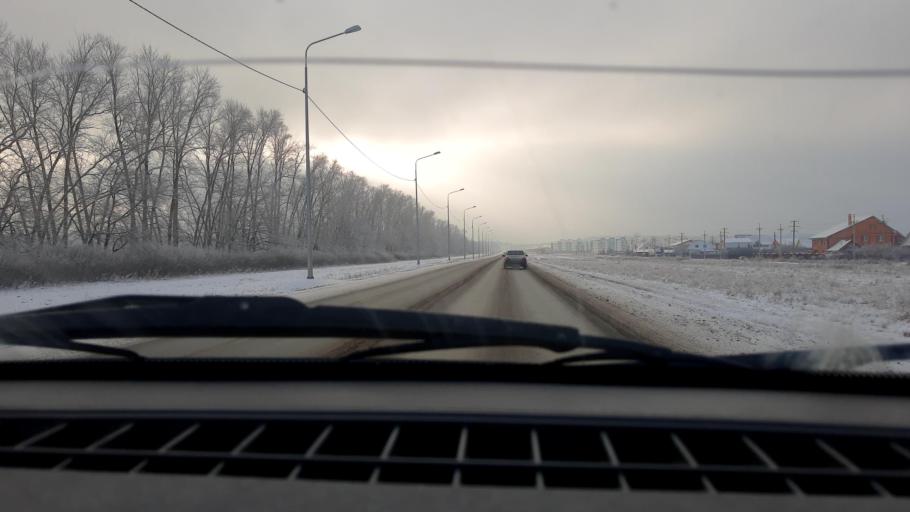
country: RU
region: Bashkortostan
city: Avdon
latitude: 54.4895
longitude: 55.8983
